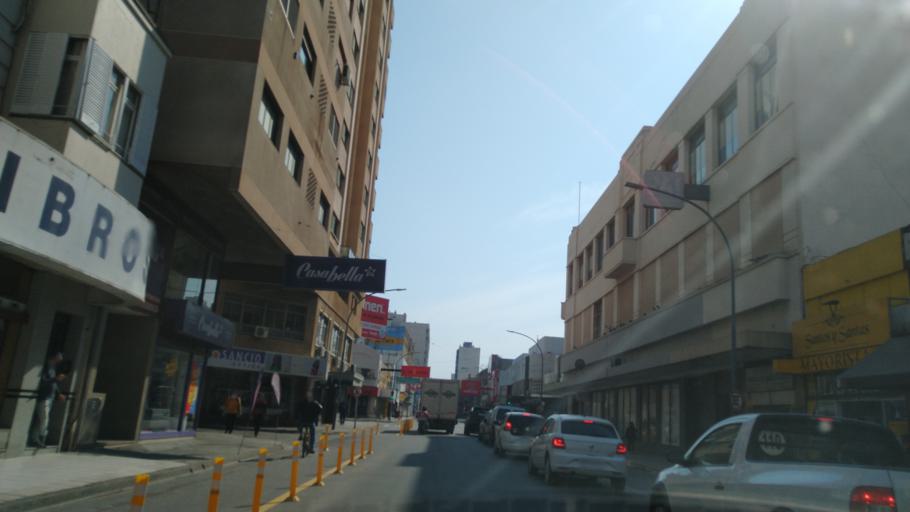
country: AR
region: Buenos Aires
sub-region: Partido de Bahia Blanca
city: Bahia Blanca
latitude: -38.7212
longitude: -62.2667
